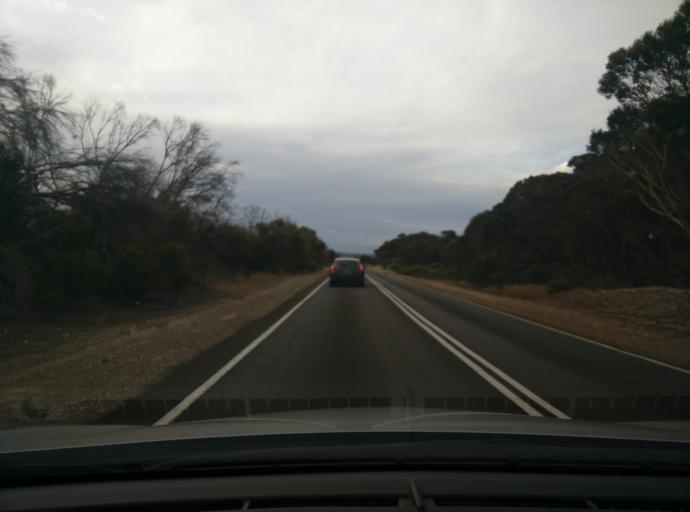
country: AU
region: South Australia
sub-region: Kangaroo Island
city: Kingscote
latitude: -35.7644
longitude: 137.6145
